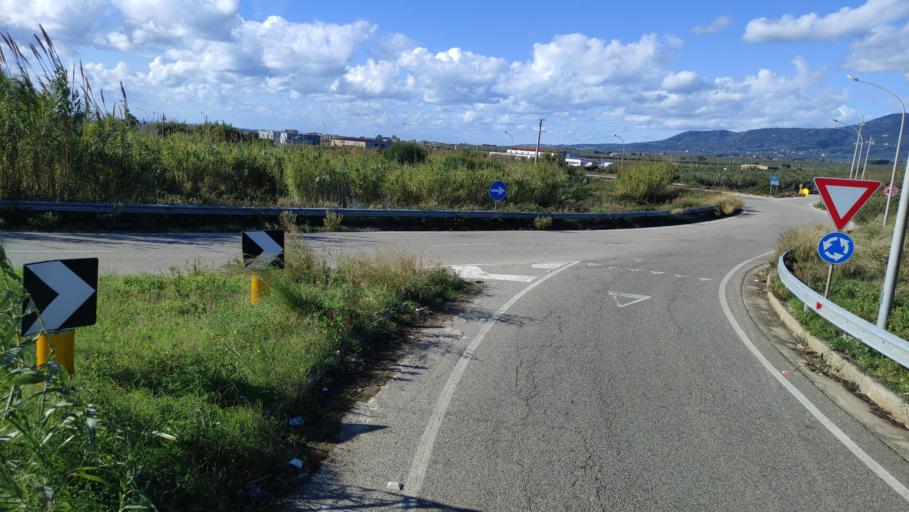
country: IT
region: Calabria
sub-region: Provincia di Catanzaro
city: Santa Eufemia Lamezia
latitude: 38.9203
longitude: 16.2746
